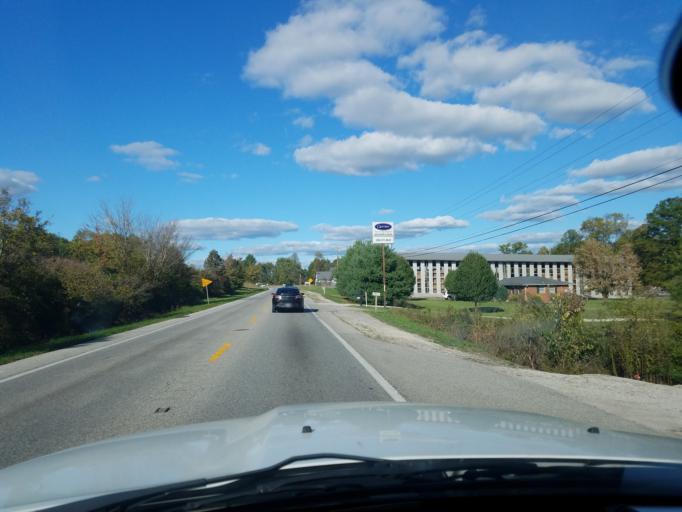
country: US
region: Kentucky
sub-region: Laurel County
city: London
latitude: 37.0450
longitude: -84.0536
